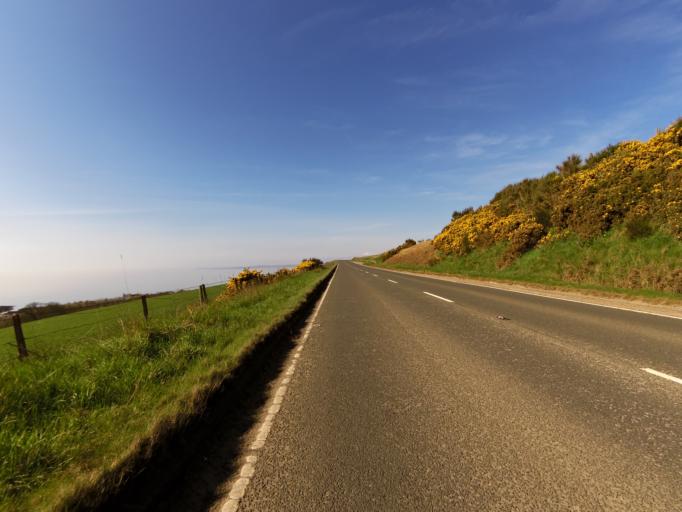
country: GB
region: Scotland
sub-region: Aberdeenshire
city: Inverbervie
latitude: 56.7973
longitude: -2.3384
